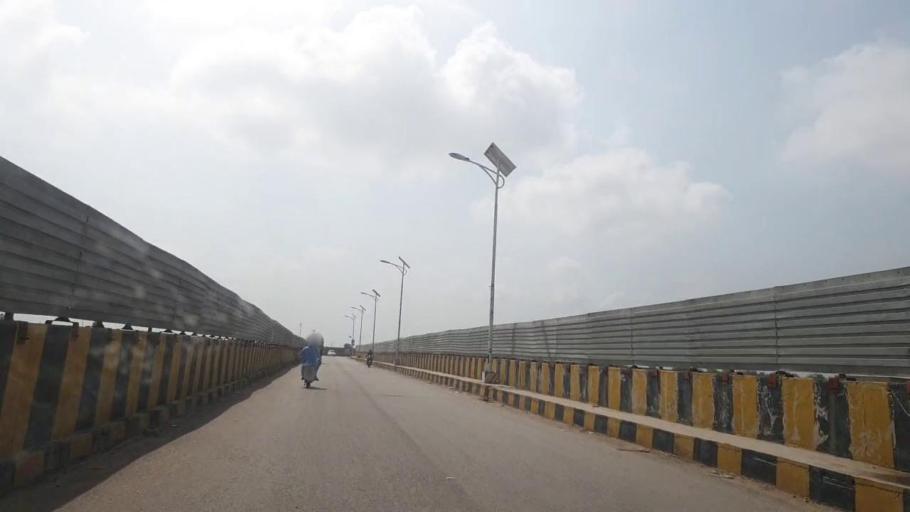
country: PK
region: Sindh
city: Khairpur
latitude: 27.5282
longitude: 68.7423
